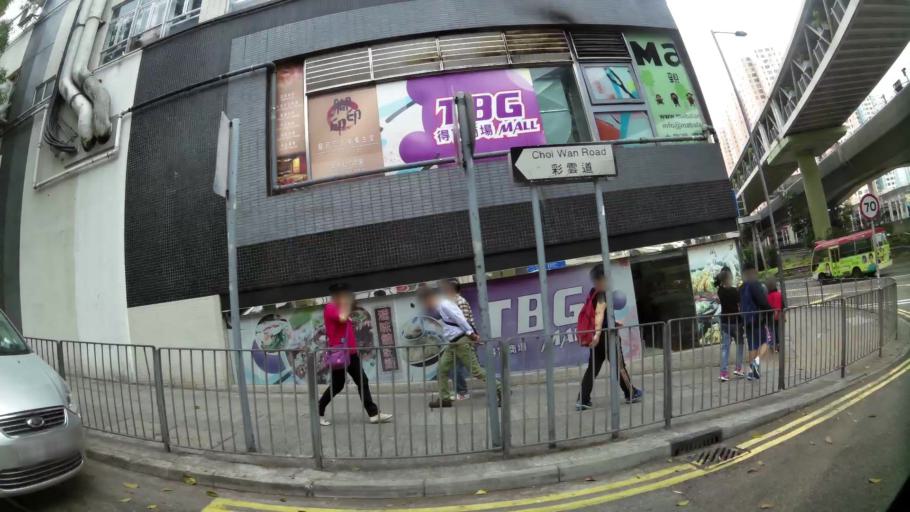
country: HK
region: Kowloon City
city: Kowloon
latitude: 22.3272
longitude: 114.2139
